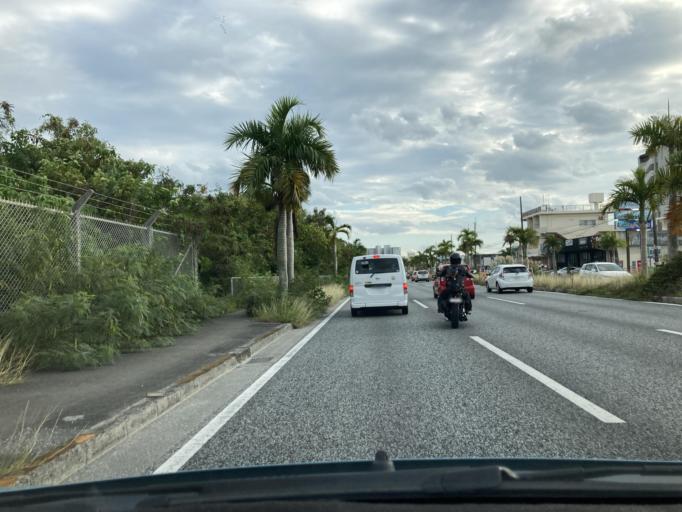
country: JP
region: Okinawa
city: Chatan
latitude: 26.3342
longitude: 127.7516
